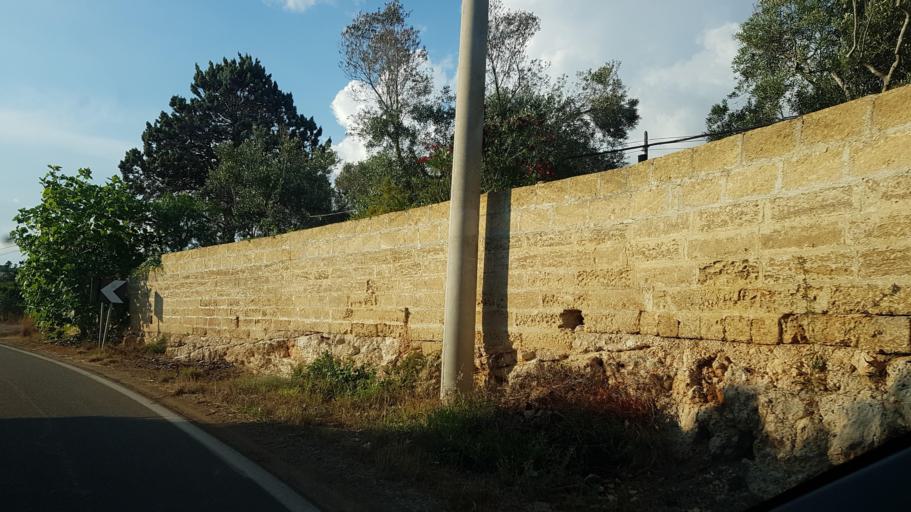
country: IT
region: Apulia
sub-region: Provincia di Lecce
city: Gemini
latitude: 39.8505
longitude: 18.2092
